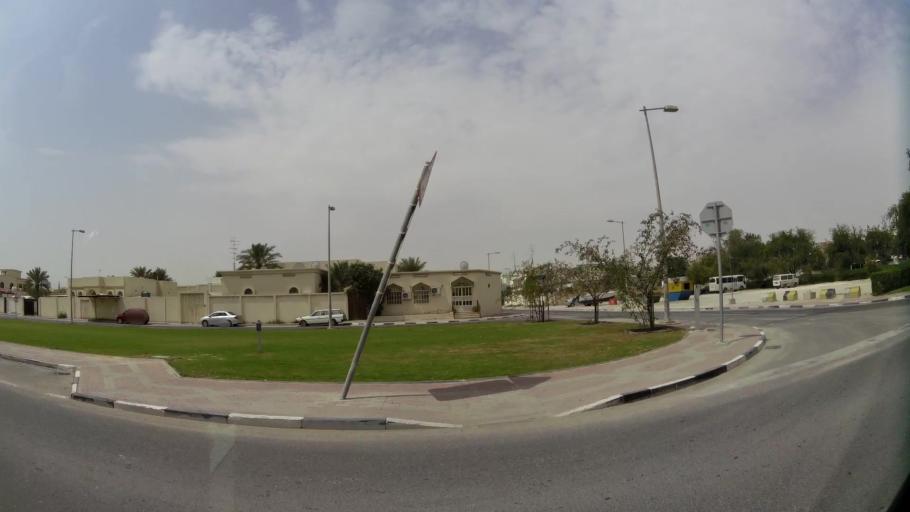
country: QA
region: Baladiyat ad Dawhah
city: Doha
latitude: 25.3135
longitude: 51.4788
